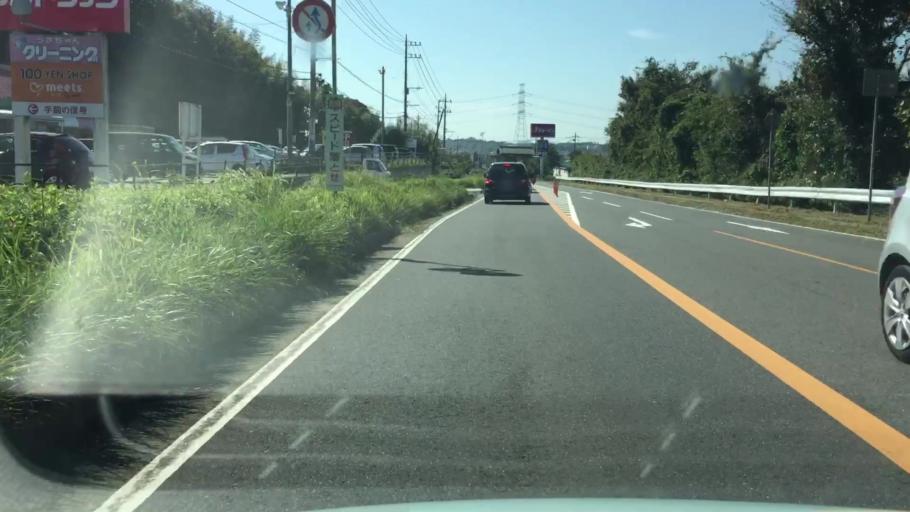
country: JP
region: Ibaraki
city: Ryugasaki
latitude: 35.8758
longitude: 140.1560
